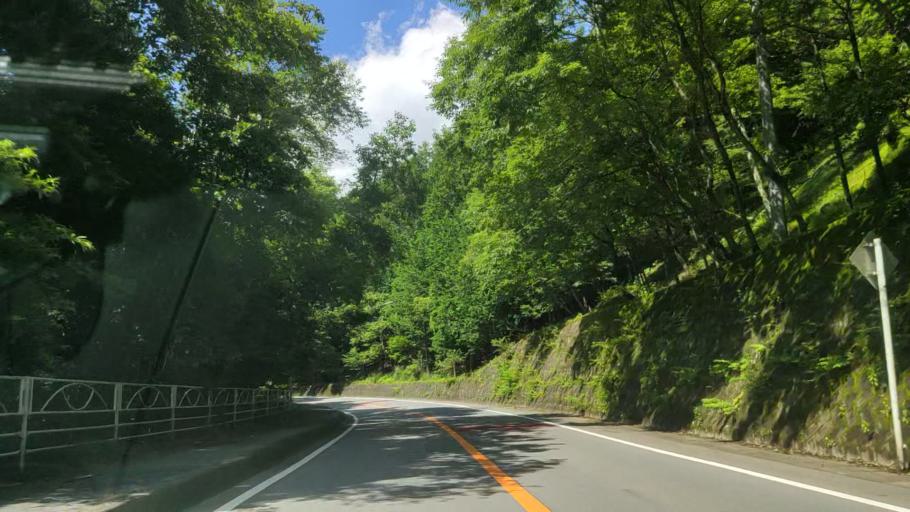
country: JP
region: Yamanashi
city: Enzan
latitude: 35.8553
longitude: 138.7576
